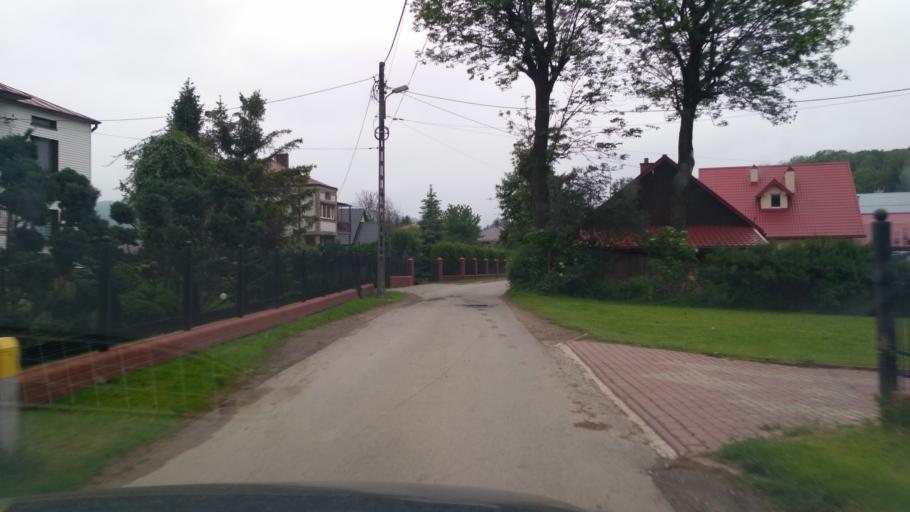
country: PL
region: Subcarpathian Voivodeship
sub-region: Powiat rzeszowski
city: Dynow
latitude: 49.8125
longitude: 22.2360
